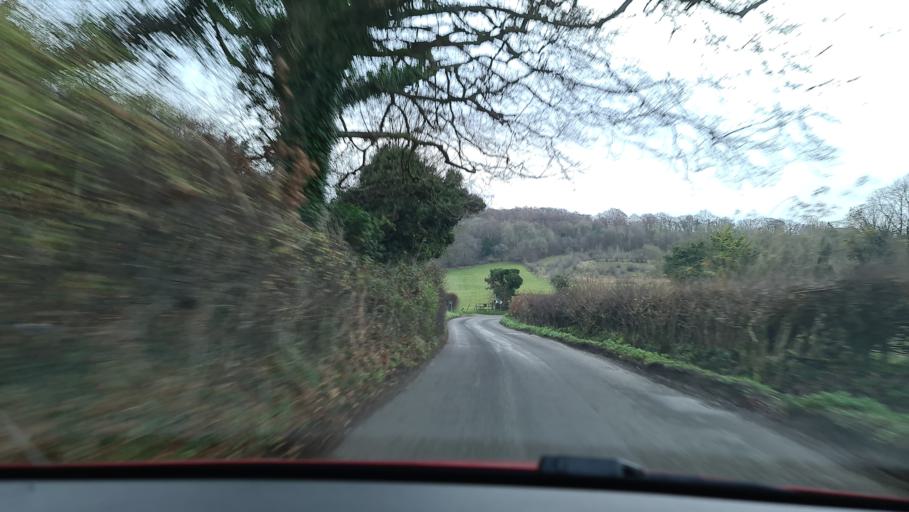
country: GB
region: England
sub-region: Buckinghamshire
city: Princes Risborough
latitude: 51.7144
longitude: -0.8131
